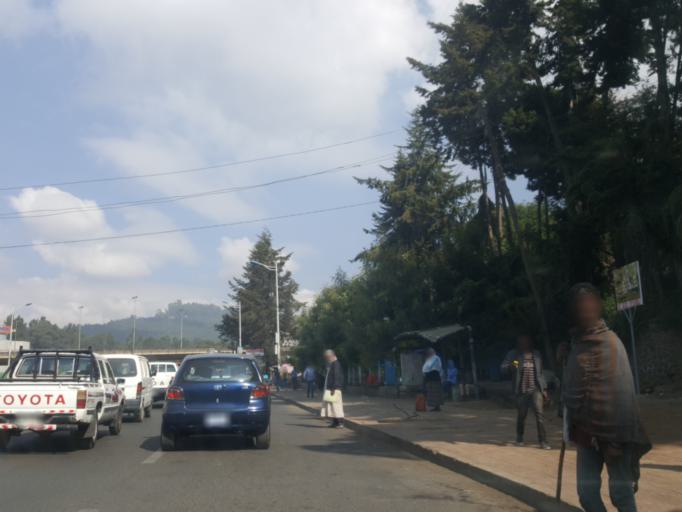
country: ET
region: Adis Abeba
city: Addis Ababa
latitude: 9.0555
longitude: 38.7139
